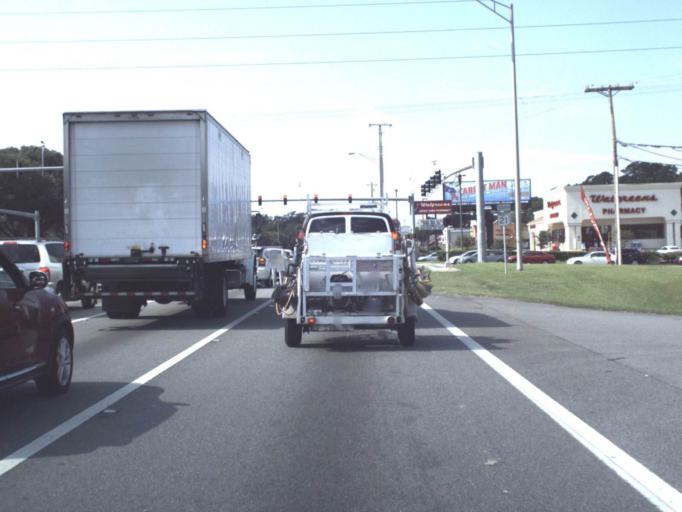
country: US
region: Florida
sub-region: Clay County
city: Bellair-Meadowbrook Terrace
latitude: 30.1877
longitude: -81.7395
